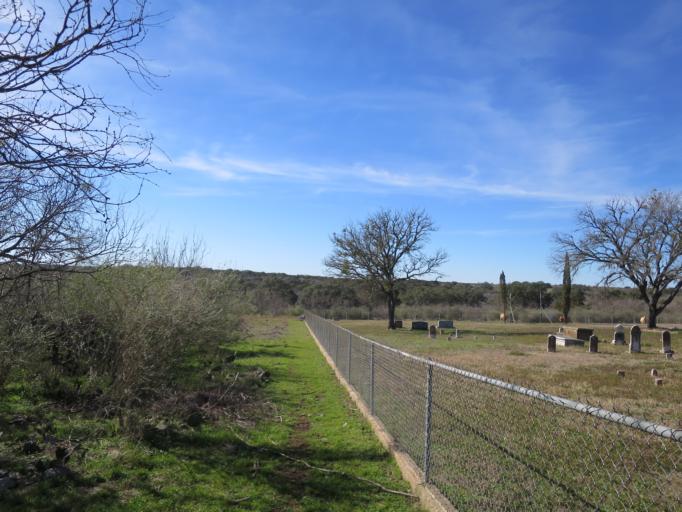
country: US
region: Texas
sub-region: Burnet County
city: Marble Falls
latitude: 30.5014
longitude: -98.1971
